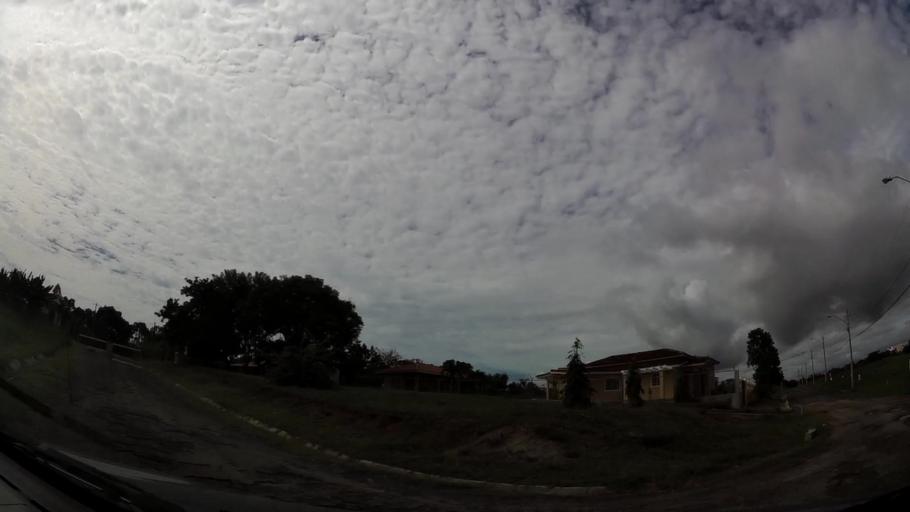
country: PA
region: Panama
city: Nueva Gorgona
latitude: 8.5450
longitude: -79.8882
